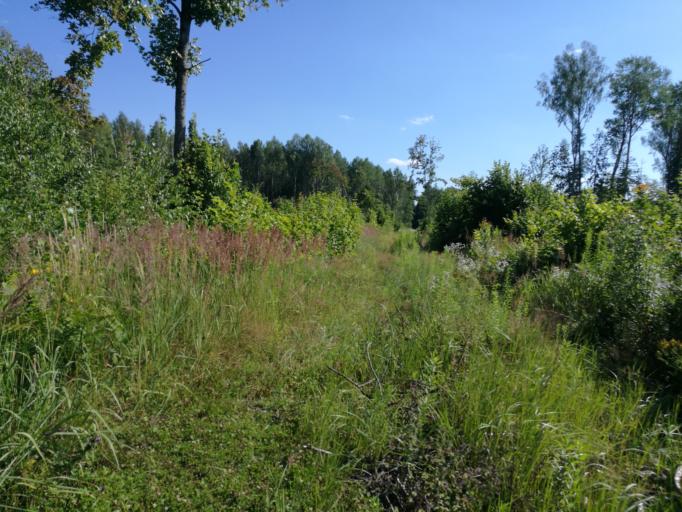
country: BY
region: Minsk
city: Krupki
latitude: 54.0743
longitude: 29.1946
